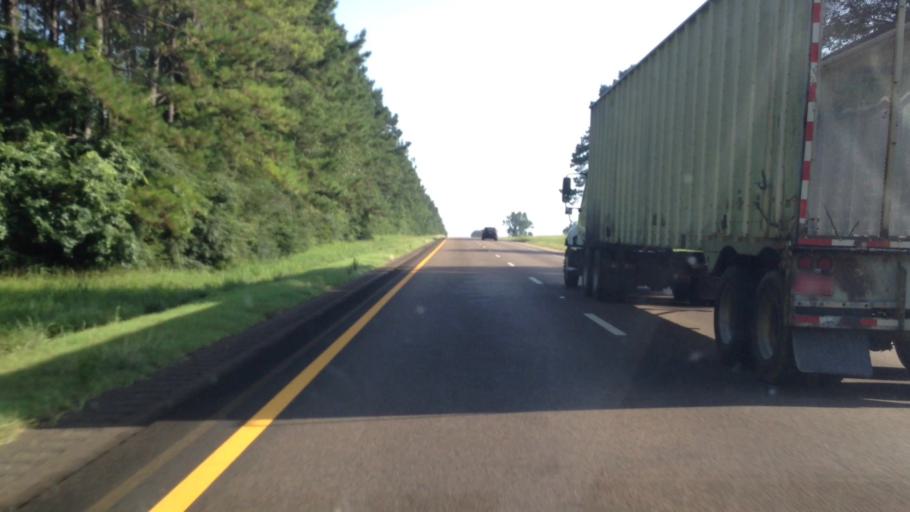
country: US
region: Mississippi
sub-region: Pike County
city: Summit
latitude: 31.3066
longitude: -90.4779
